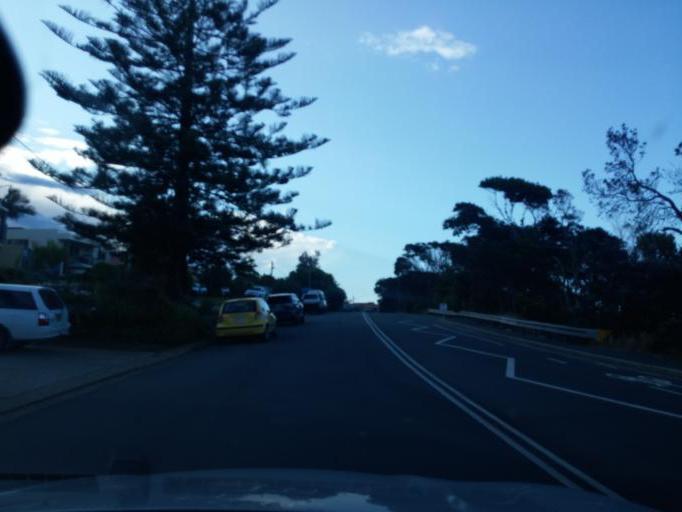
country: AU
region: New South Wales
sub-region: Port Macquarie-Hastings
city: Port Macquarie
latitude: -31.4430
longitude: 152.9254
